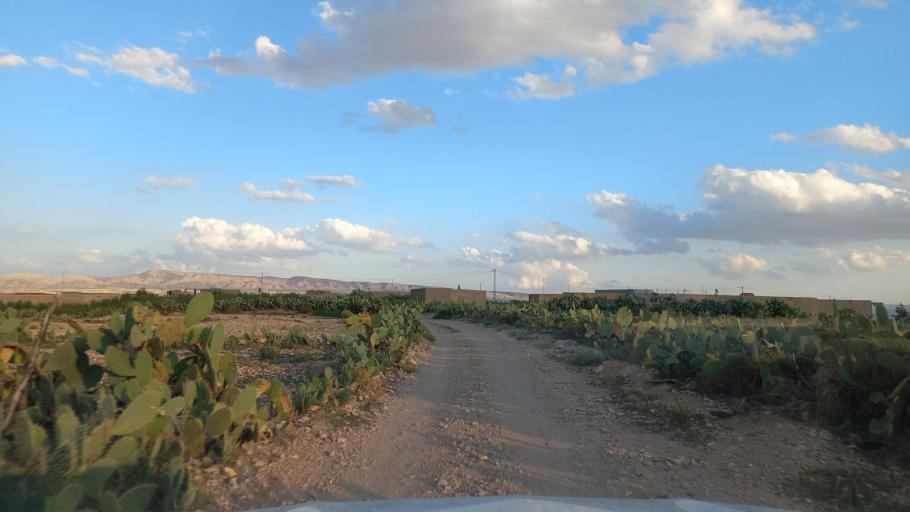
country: TN
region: Al Qasrayn
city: Sbiba
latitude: 35.3772
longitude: 9.0524
